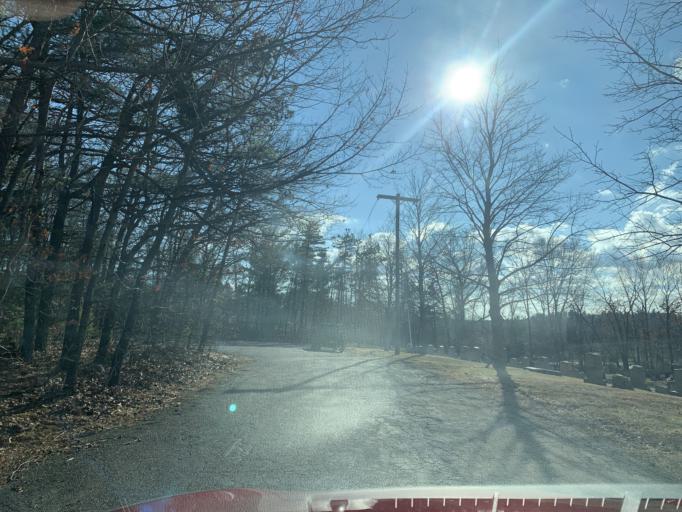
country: US
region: Massachusetts
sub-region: Essex County
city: Amesbury
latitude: 42.8418
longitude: -70.9332
